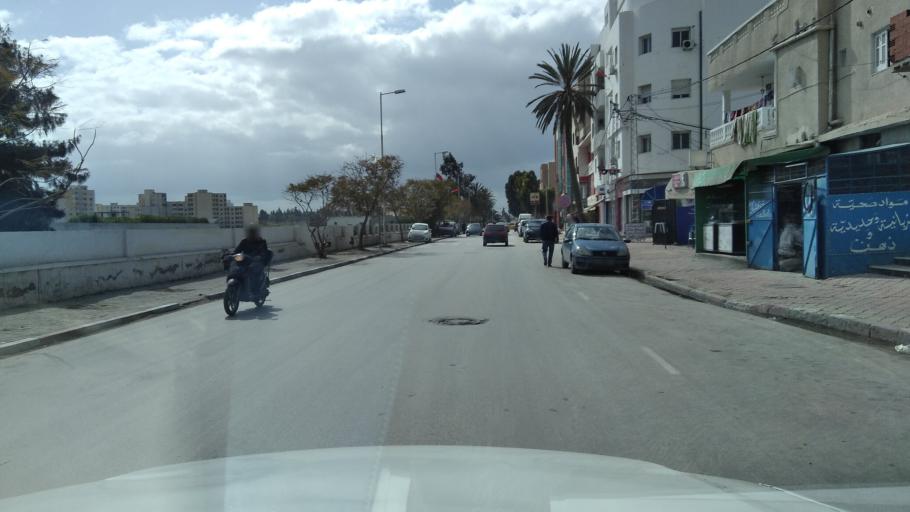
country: TN
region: Bin 'Arus
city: Ben Arous
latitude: 36.7505
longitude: 10.2245
